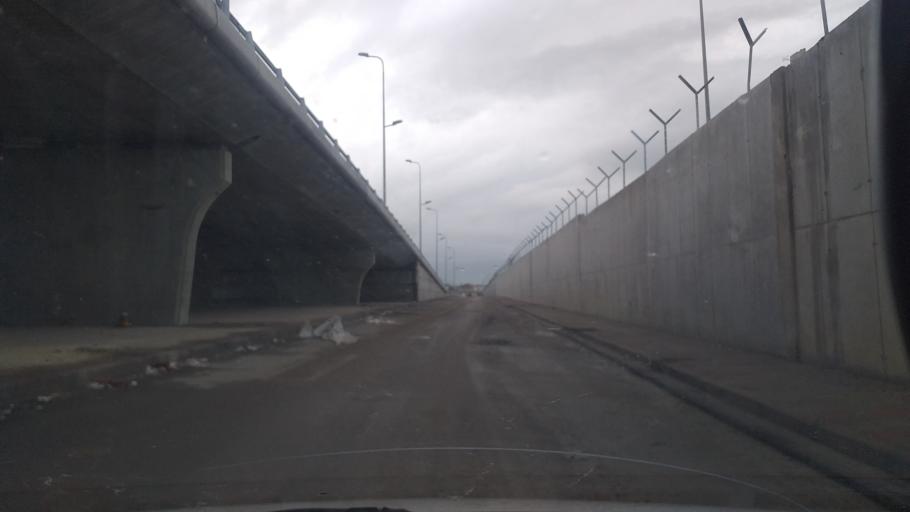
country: TN
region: Ariana
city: Ariana
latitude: 36.8521
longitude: 10.2122
